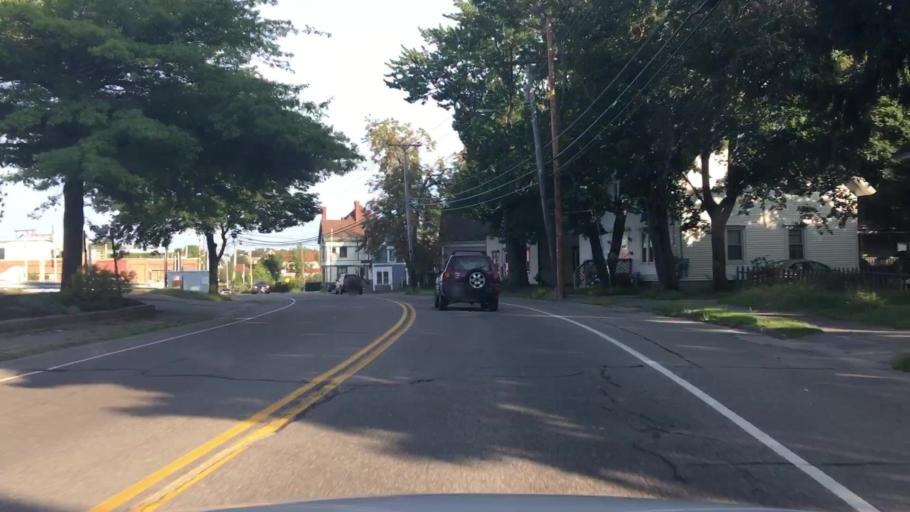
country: US
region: Maine
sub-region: Cumberland County
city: Westbrook
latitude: 43.6841
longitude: -70.3548
